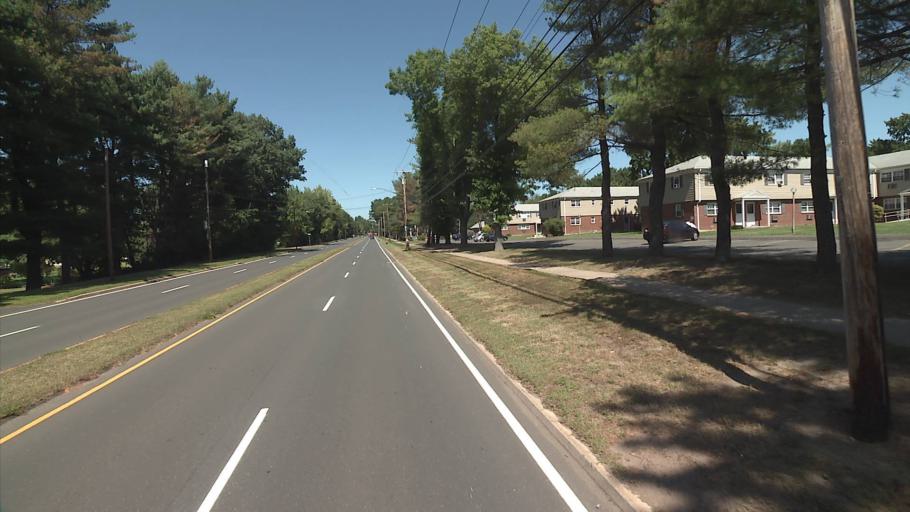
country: US
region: Connecticut
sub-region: Hartford County
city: Windsor
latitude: 41.8244
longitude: -72.6563
